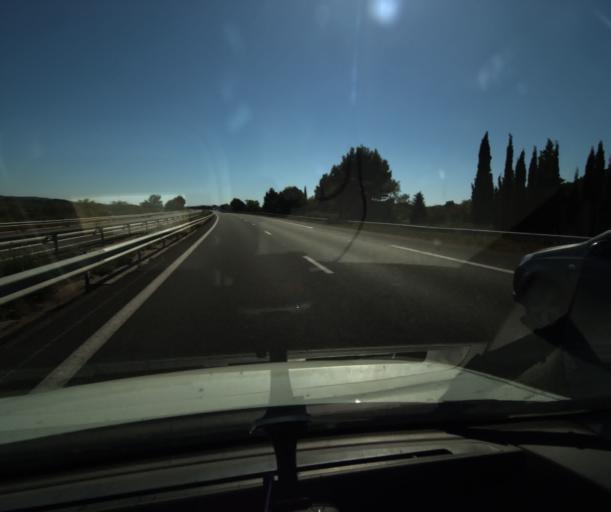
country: FR
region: Languedoc-Roussillon
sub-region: Departement de l'Aude
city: Fabrezan
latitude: 43.1721
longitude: 2.6809
